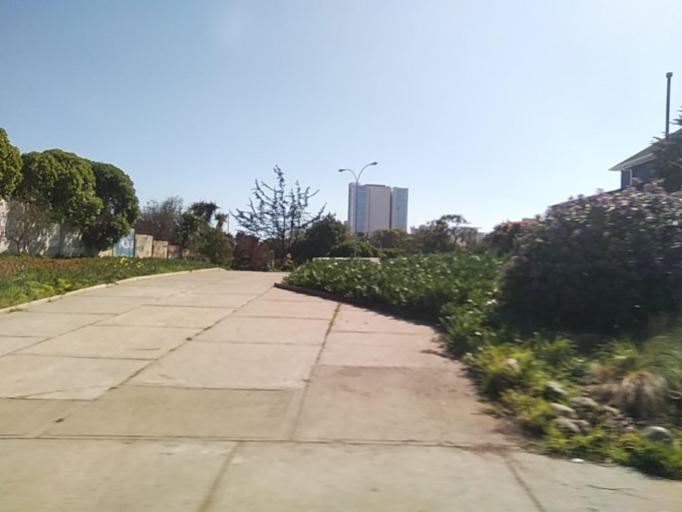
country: CL
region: Valparaiso
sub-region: Provincia de Valparaiso
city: Vina del Mar
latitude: -32.9399
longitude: -71.5432
